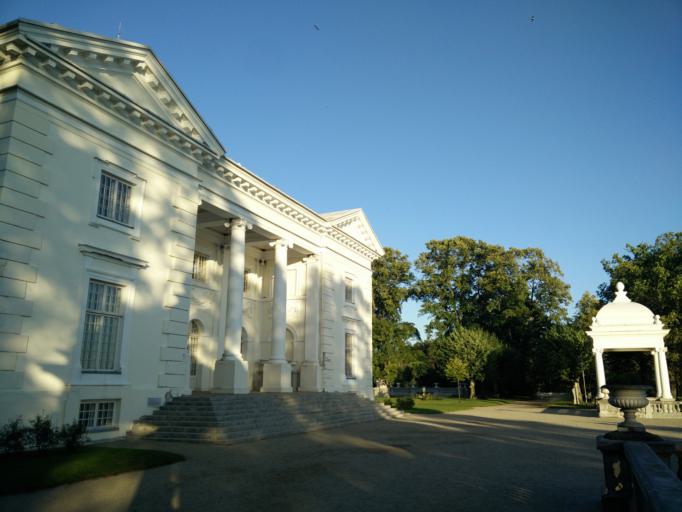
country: LT
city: Trakai
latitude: 54.6598
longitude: 24.9431
